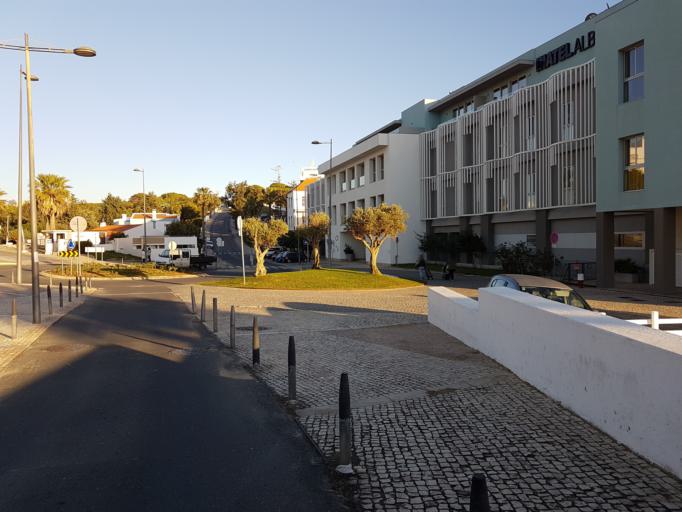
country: PT
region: Faro
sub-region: Albufeira
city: Albufeira
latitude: 37.0863
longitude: -8.2444
